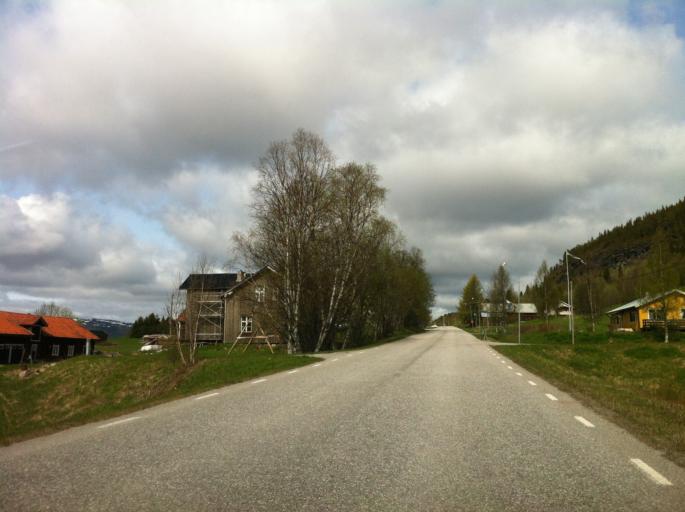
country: NO
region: Hedmark
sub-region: Engerdal
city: Engerdal
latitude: 62.4403
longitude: 12.7112
